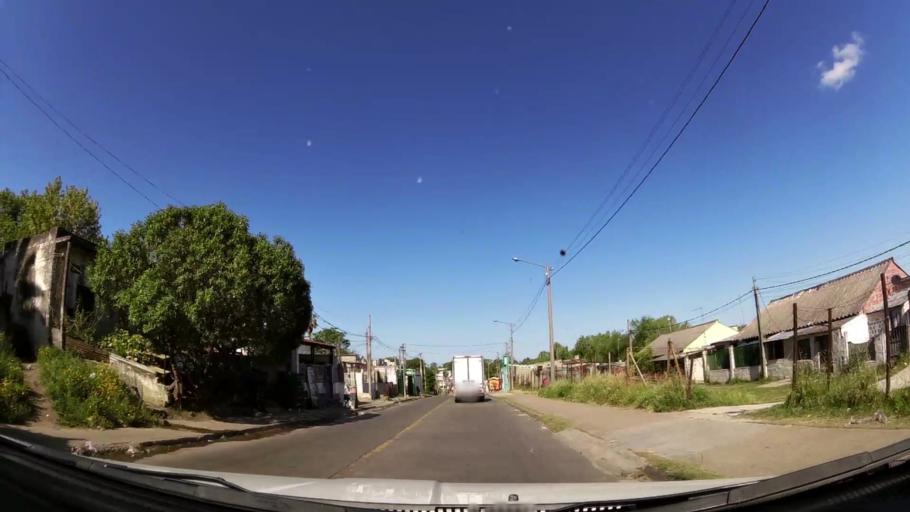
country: UY
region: Montevideo
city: Montevideo
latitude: -34.8354
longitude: -56.1662
